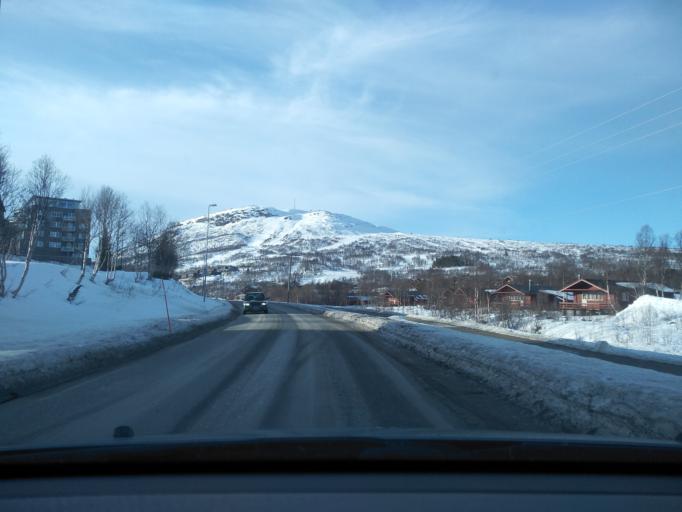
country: NO
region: Aust-Agder
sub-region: Bykle
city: Hovden
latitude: 59.5671
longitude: 7.3637
